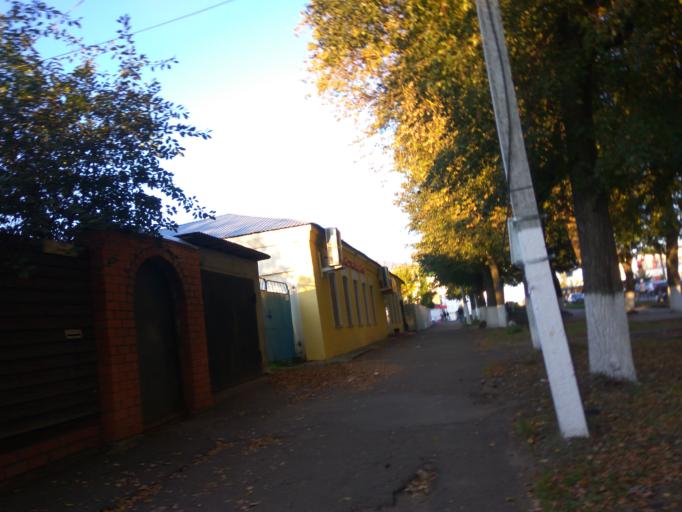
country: RU
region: Moskovskaya
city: Yegor'yevsk
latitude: 55.3788
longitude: 39.0404
